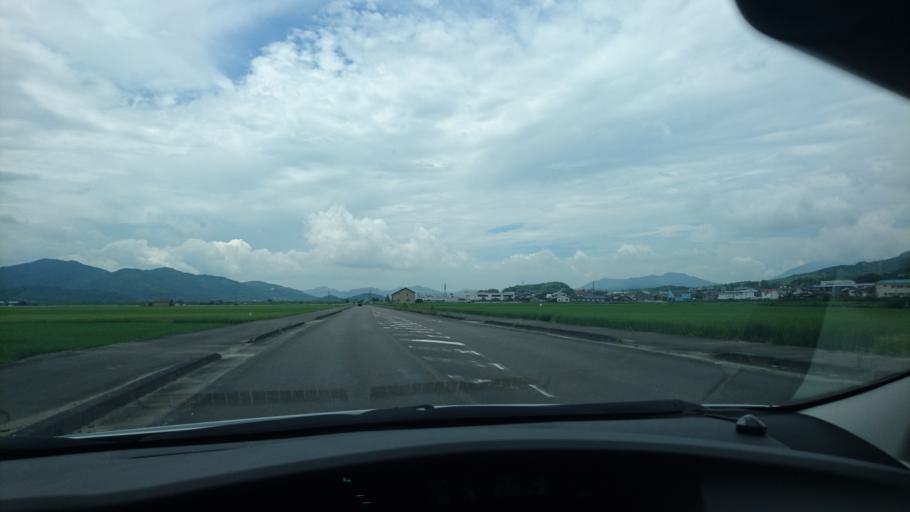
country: JP
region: Saga Prefecture
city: Takeocho-takeo
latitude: 33.2103
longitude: 130.1204
